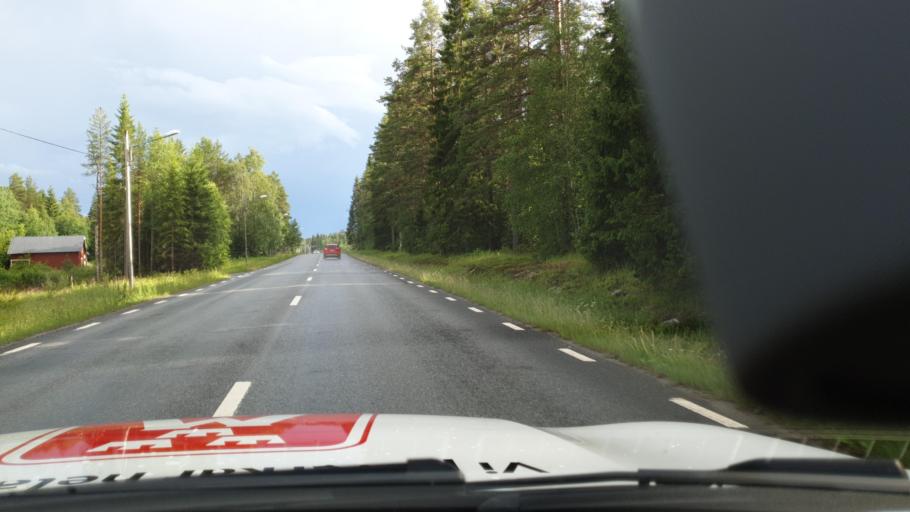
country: SE
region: Vaesterbotten
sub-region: Umea Kommun
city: Ersmark
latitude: 63.8746
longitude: 20.3047
